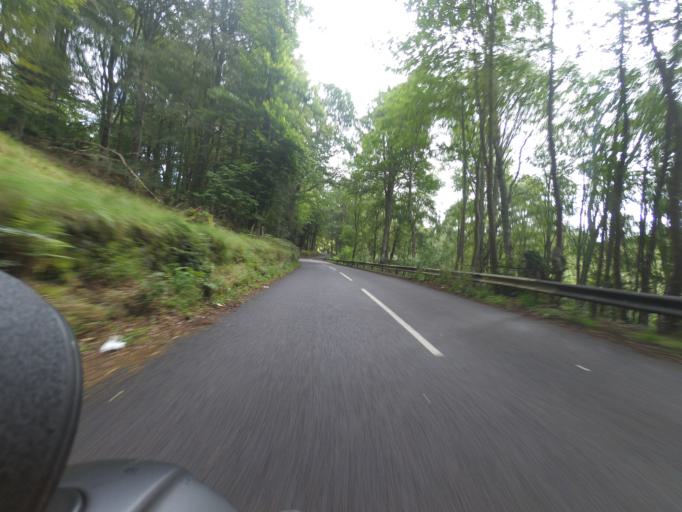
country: GB
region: Scotland
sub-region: Perth and Kinross
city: Bankfoot
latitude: 56.5710
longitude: -3.5819
